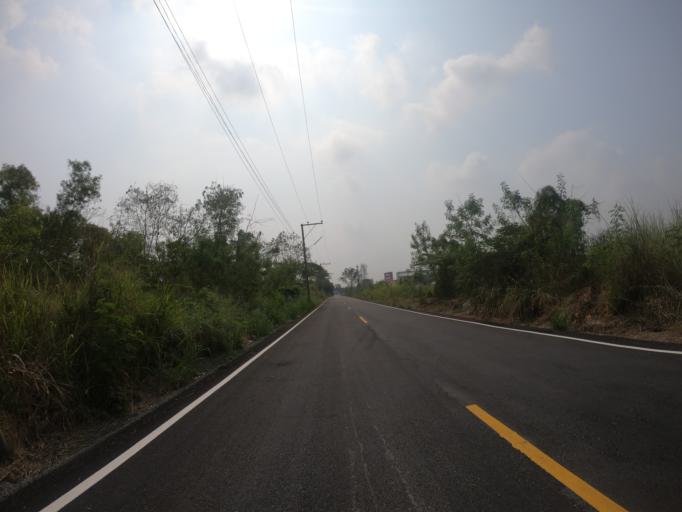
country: TH
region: Pathum Thani
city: Nong Suea
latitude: 14.0641
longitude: 100.8493
